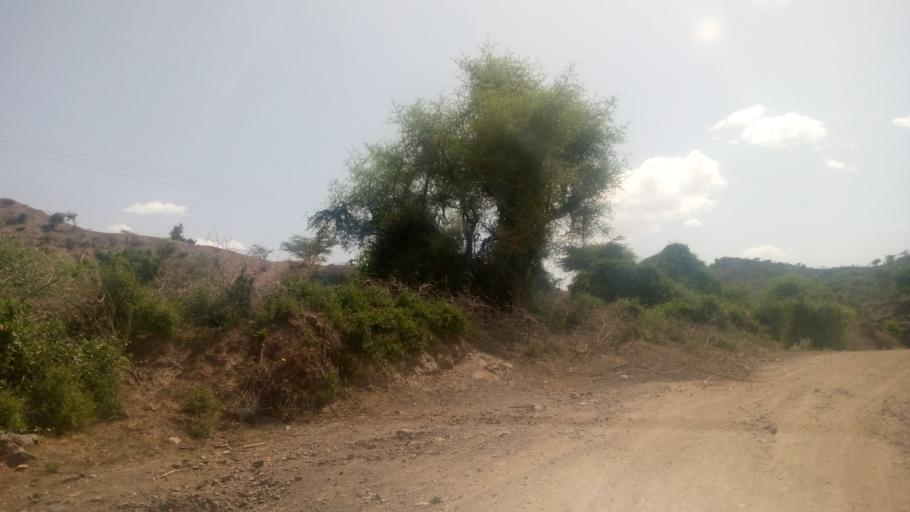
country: ET
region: Oromiya
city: Deder
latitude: 9.4988
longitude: 41.2565
